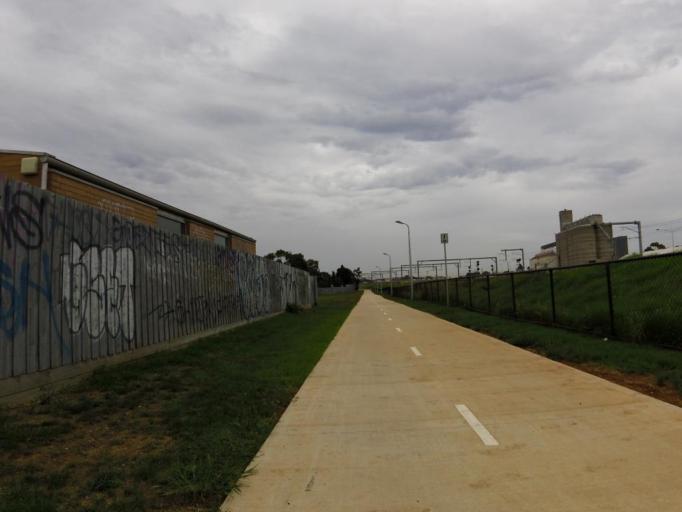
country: AU
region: Victoria
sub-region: Brimbank
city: Sunshine West
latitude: -37.7913
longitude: 144.8356
